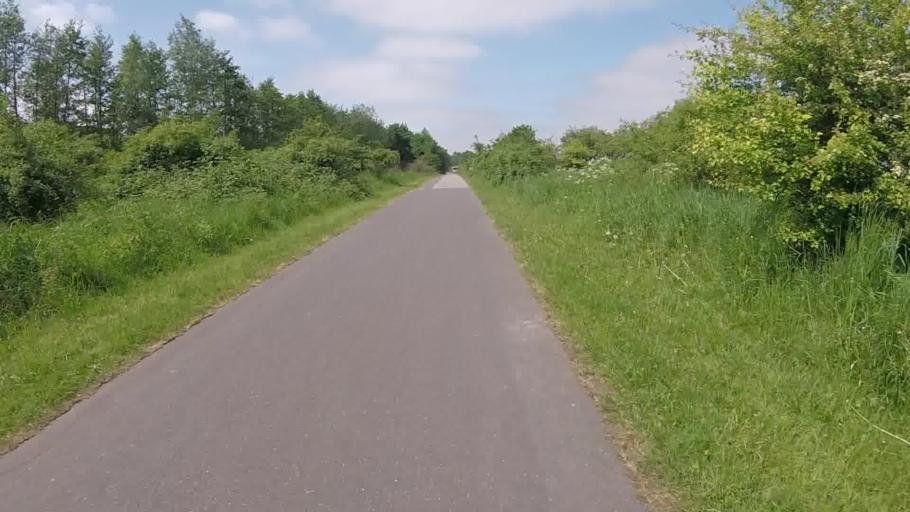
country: DE
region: Schleswig-Holstein
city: Oststeinbek
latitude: 53.4904
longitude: 10.1623
